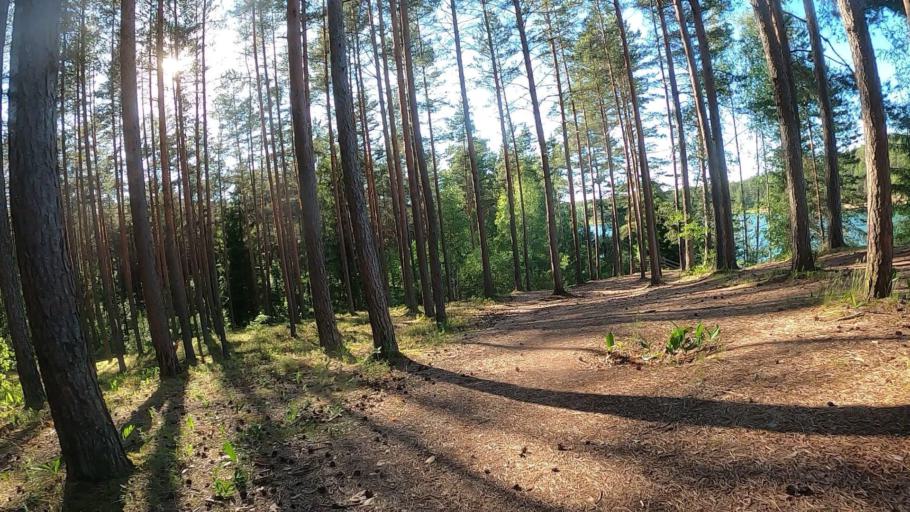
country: LV
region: Ikskile
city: Ikskile
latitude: 56.8371
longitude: 24.5550
